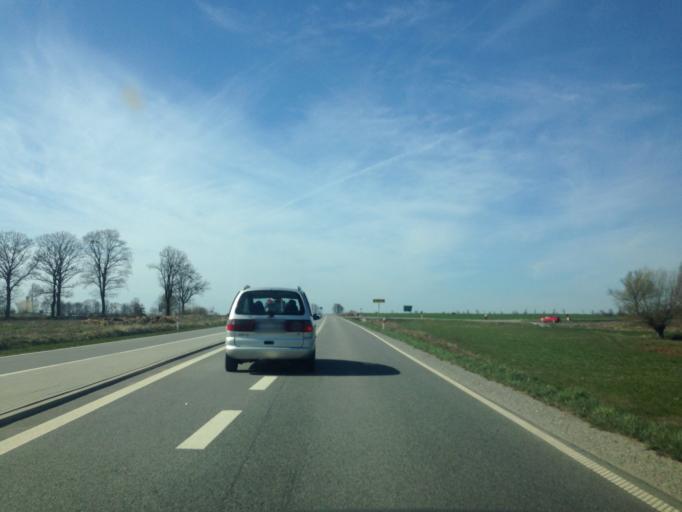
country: PL
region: Pomeranian Voivodeship
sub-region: Powiat starogardzki
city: Smetowo Graniczne
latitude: 53.7407
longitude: 18.6710
